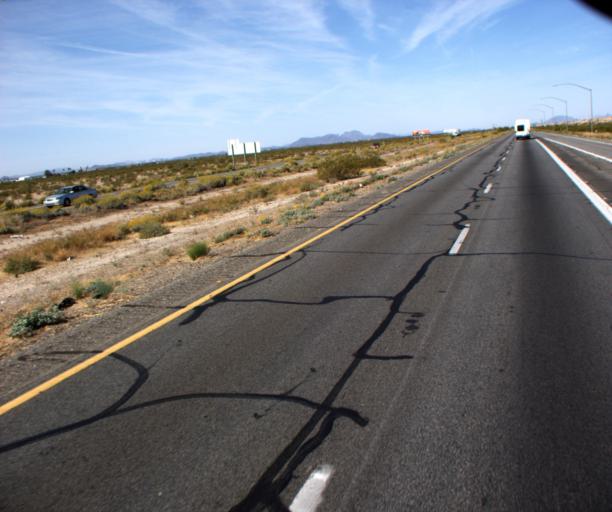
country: US
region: Arizona
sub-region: Maricopa County
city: Buckeye
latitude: 33.4405
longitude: -112.6824
